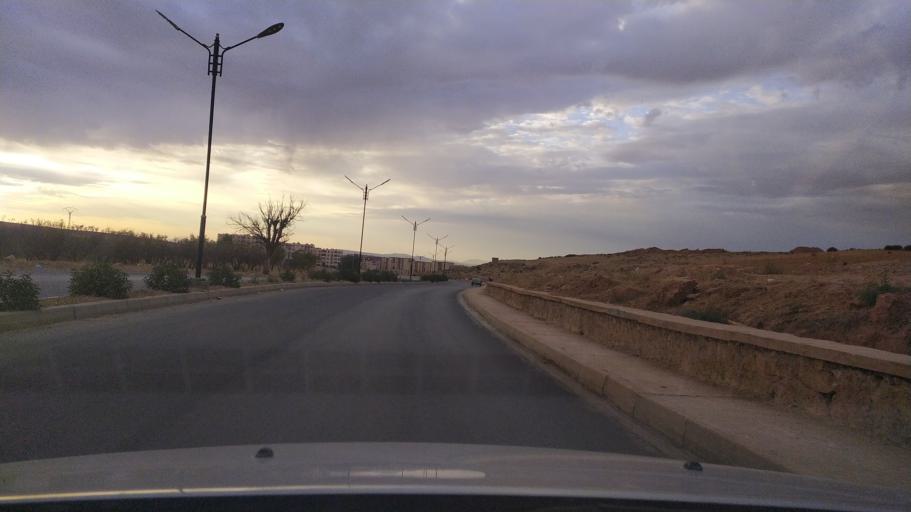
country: DZ
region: Tiaret
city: Frenda
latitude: 35.0517
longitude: 1.0680
